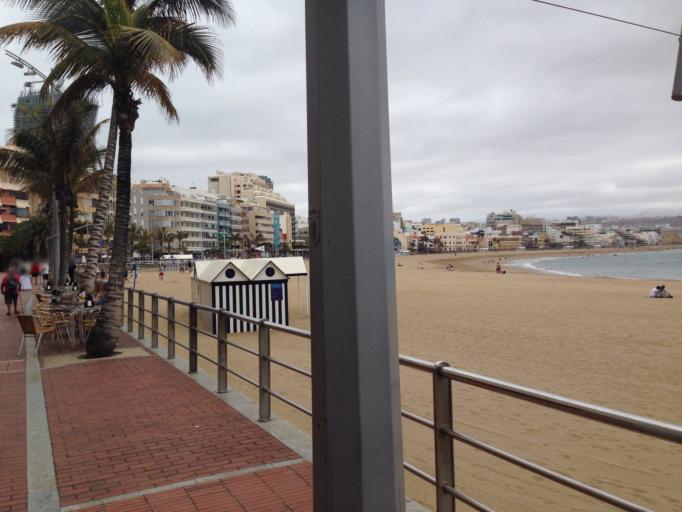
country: ES
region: Canary Islands
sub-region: Provincia de Las Palmas
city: Las Palmas de Gran Canaria
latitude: 28.1482
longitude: -15.4306
